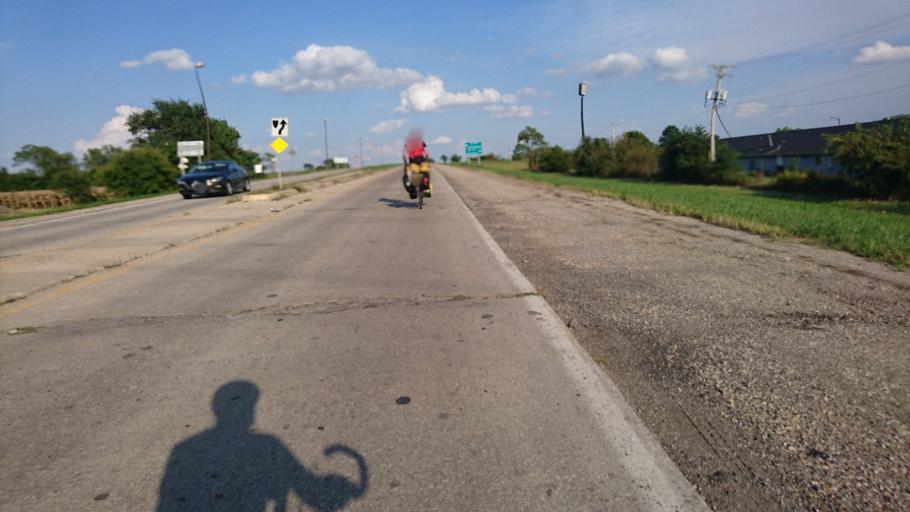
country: US
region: Illinois
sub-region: Logan County
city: Atlanta
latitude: 40.2596
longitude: -89.2248
